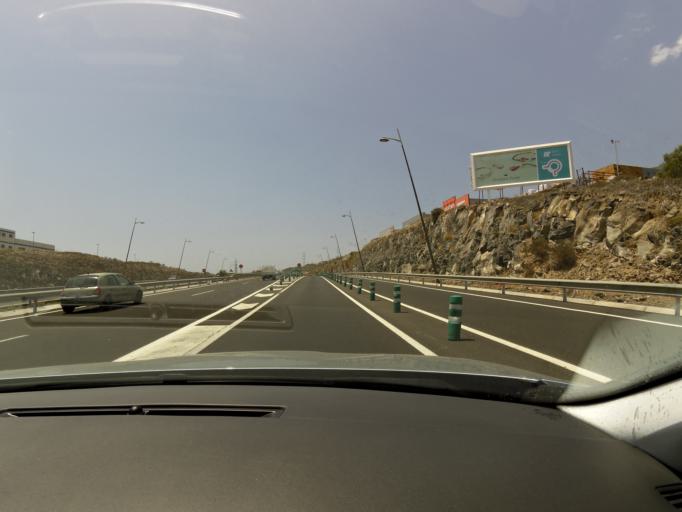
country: ES
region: Canary Islands
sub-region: Provincia de Santa Cruz de Tenerife
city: Adeje
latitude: 28.1250
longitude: -16.7420
